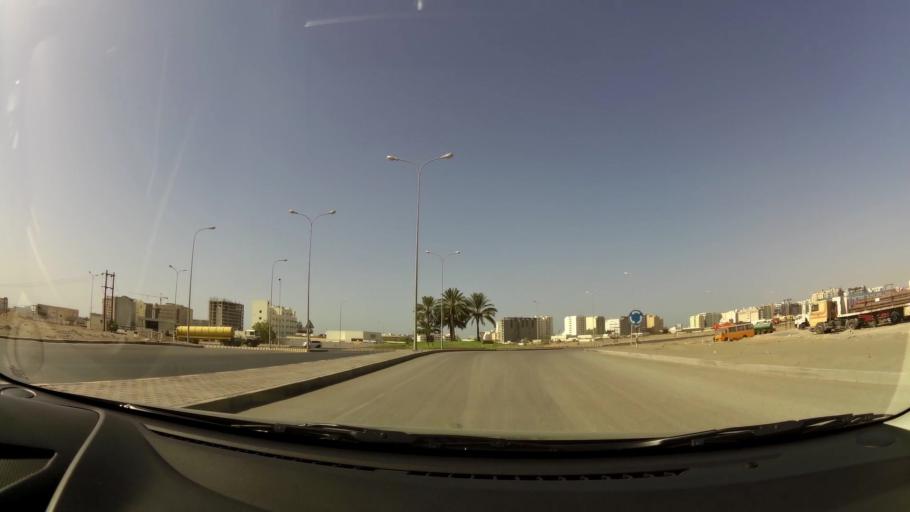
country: OM
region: Muhafazat Masqat
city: Bawshar
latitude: 23.5822
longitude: 58.3594
